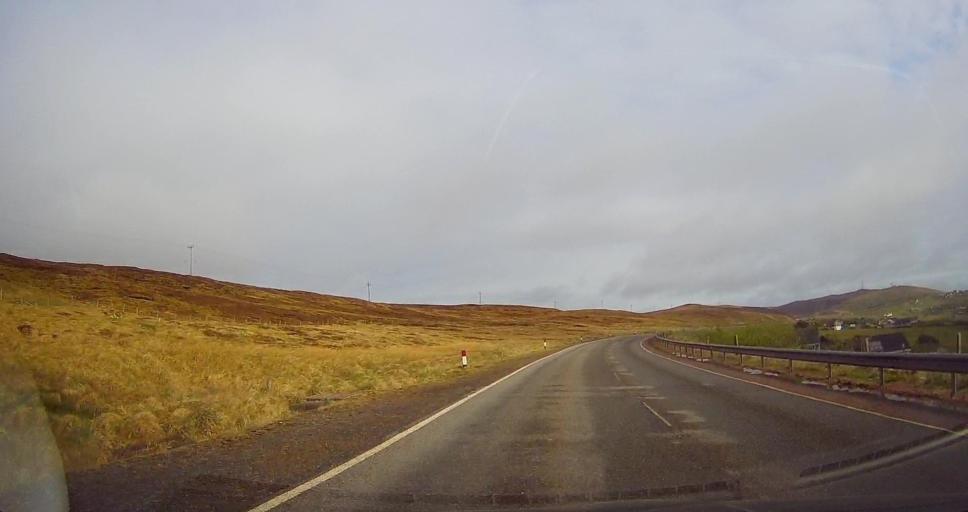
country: GB
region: Scotland
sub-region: Shetland Islands
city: Lerwick
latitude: 60.1230
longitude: -1.2166
